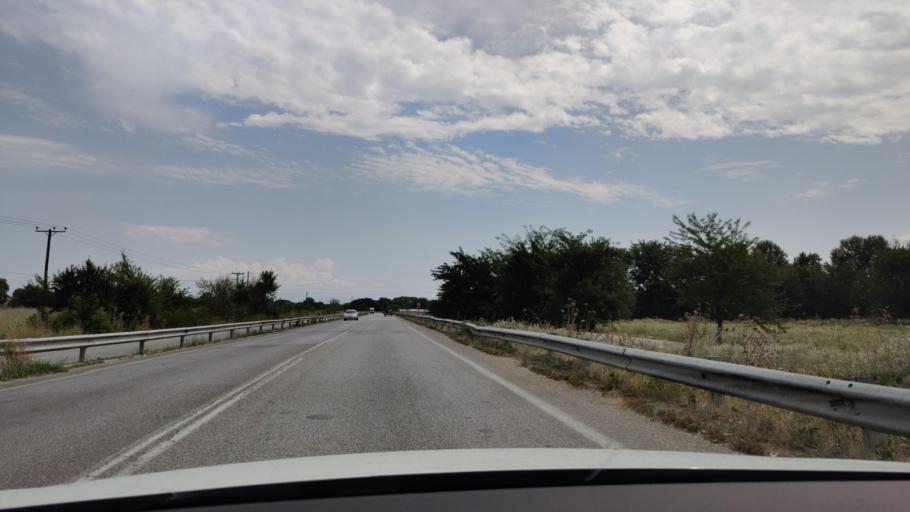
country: GR
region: Central Macedonia
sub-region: Nomos Serron
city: Serres
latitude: 41.0745
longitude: 23.5463
